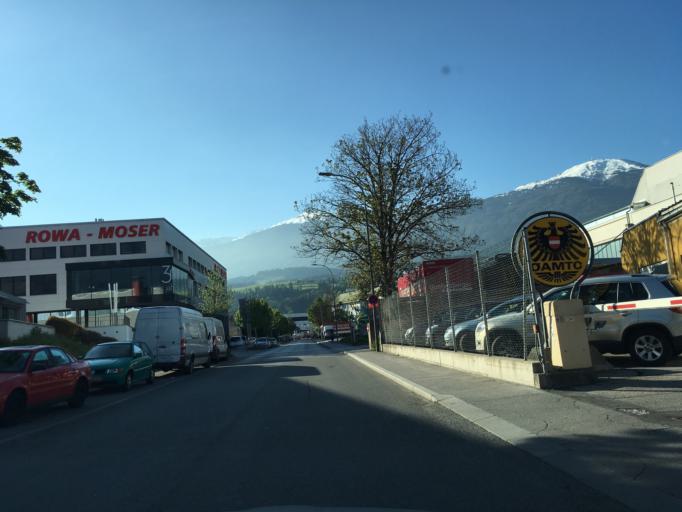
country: AT
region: Tyrol
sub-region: Politischer Bezirk Innsbruck Land
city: Ampass
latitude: 47.2663
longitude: 11.4272
